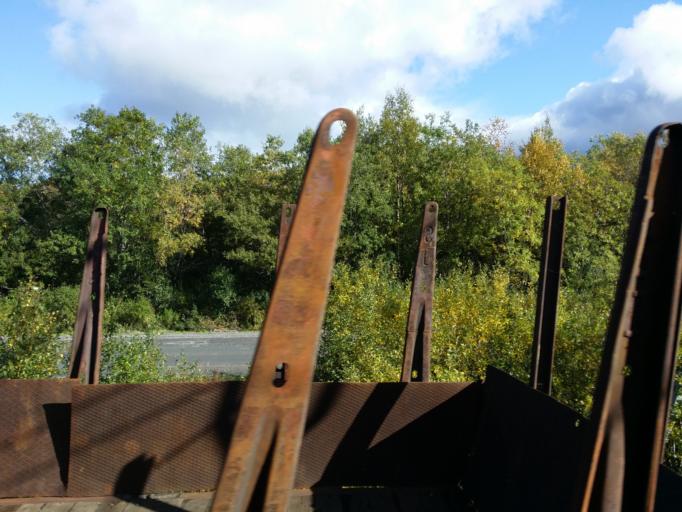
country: SE
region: Norrbotten
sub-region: Kiruna Kommun
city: Kiruna
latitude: 67.8720
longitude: 20.1947
